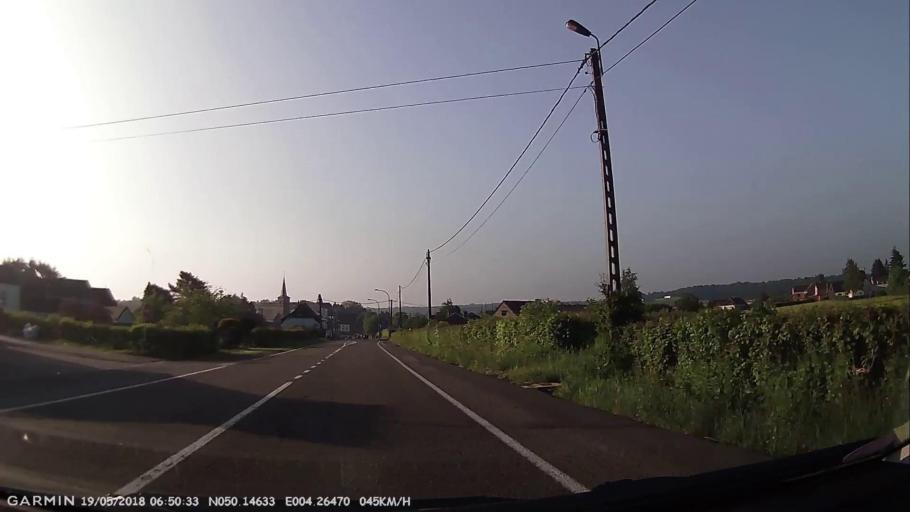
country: BE
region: Wallonia
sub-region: Province du Hainaut
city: Froidchapelle
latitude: 50.1462
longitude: 4.2649
